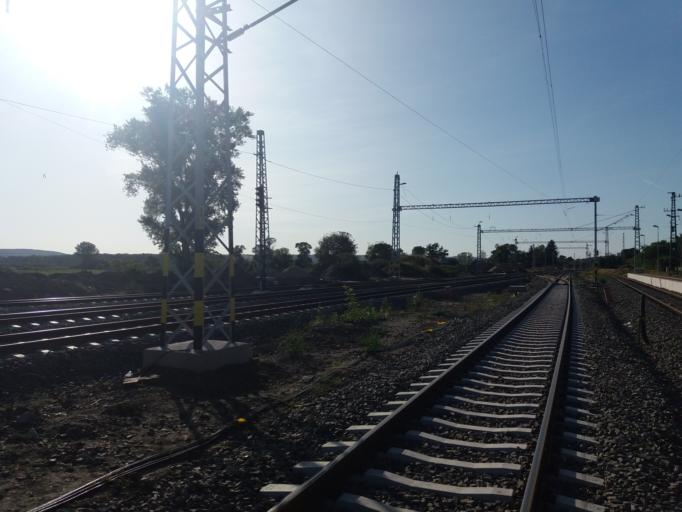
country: HU
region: Pest
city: Aszod
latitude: 47.6478
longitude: 19.4922
